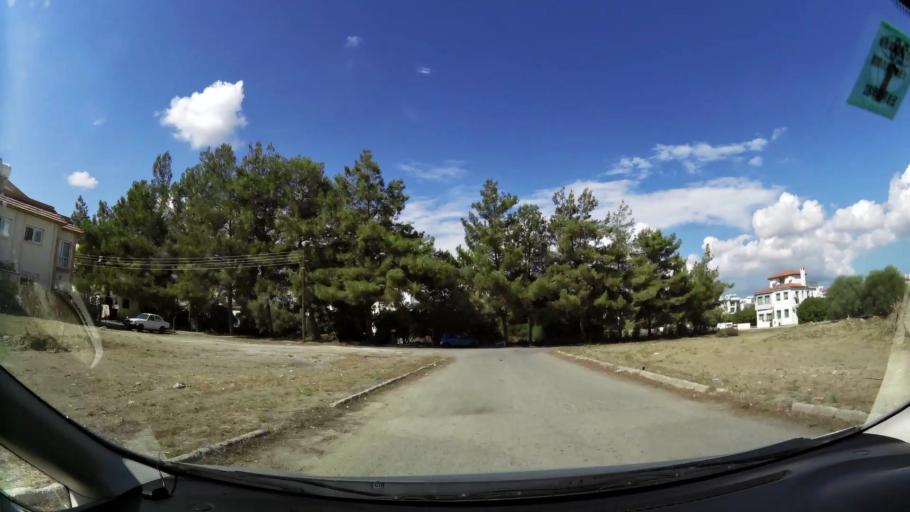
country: CY
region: Lefkosia
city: Nicosia
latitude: 35.2084
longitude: 33.3294
